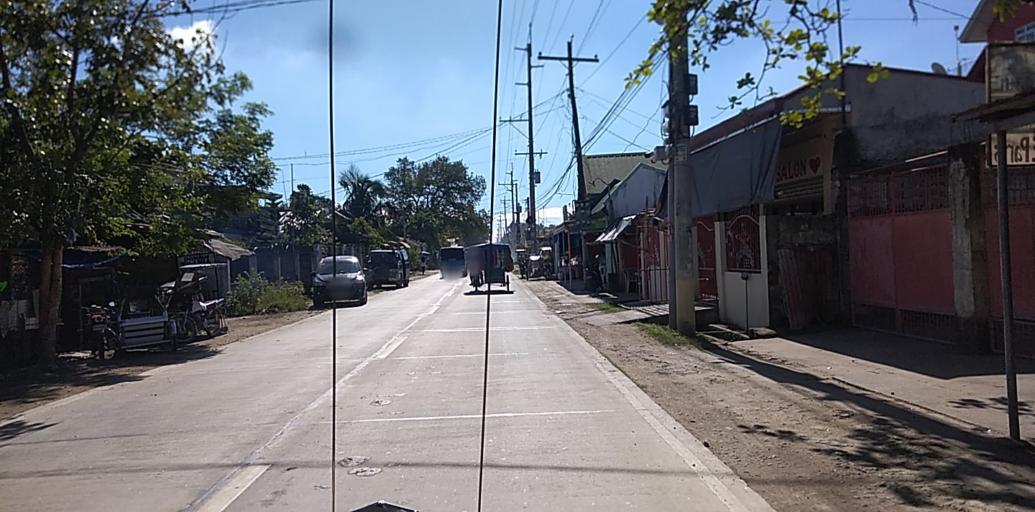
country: PH
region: Central Luzon
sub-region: Province of Pampanga
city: San Luis
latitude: 15.0572
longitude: 120.7761
